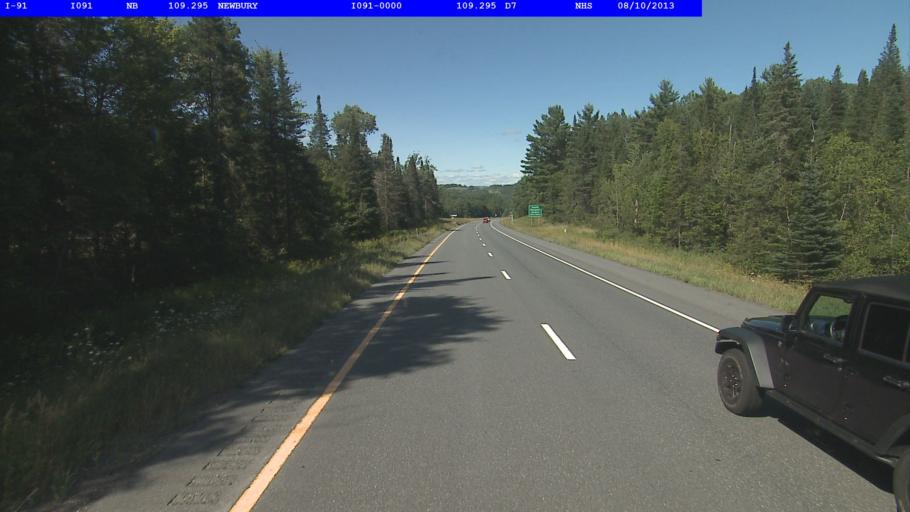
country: US
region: New Hampshire
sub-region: Grafton County
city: Woodsville
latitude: 44.1468
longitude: -72.0989
